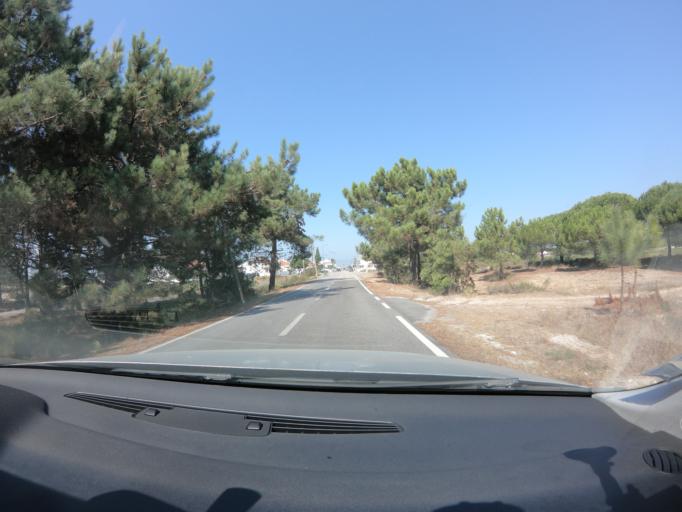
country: PT
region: Setubal
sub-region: Setubal
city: Setubal
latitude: 38.4064
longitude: -8.7470
